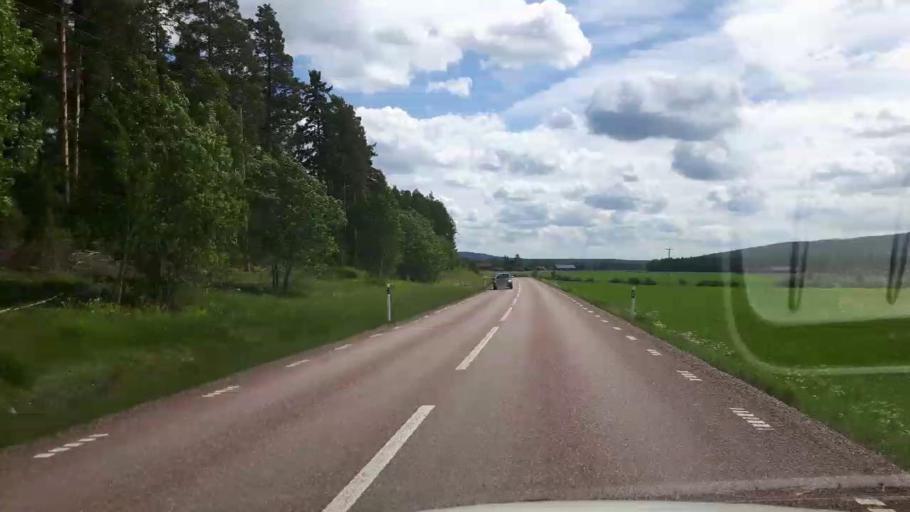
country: SE
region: Dalarna
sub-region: Saters Kommun
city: Saeter
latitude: 60.4093
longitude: 15.8607
